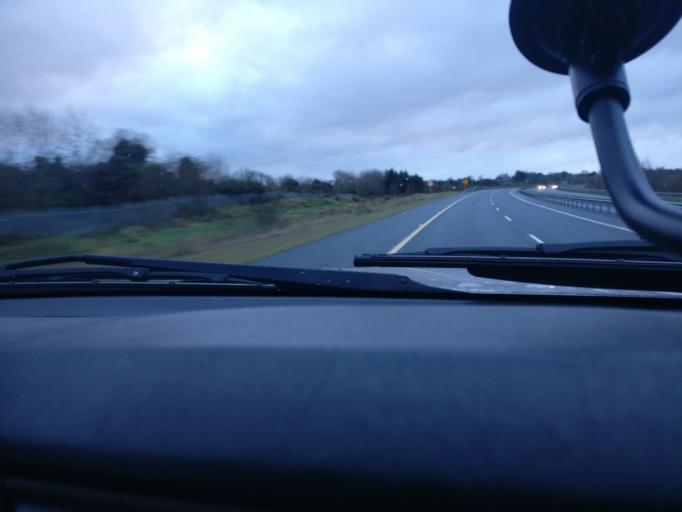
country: IE
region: Leinster
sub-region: An Iarmhi
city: Athlone
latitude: 53.4153
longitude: -7.9898
